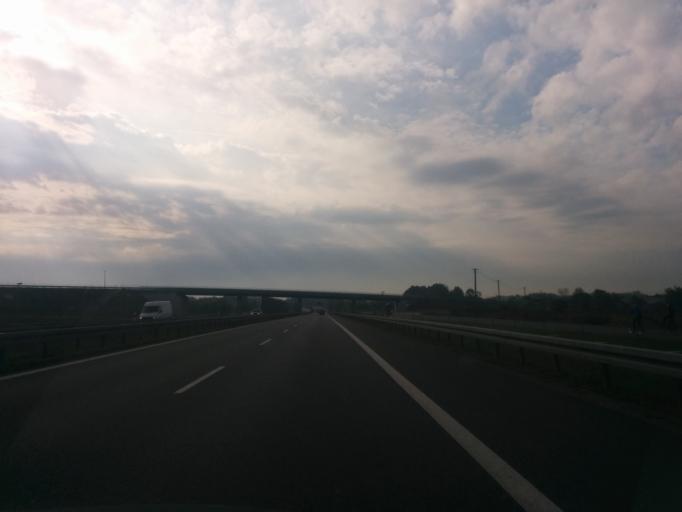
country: PL
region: Masovian Voivodeship
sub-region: Powiat bialobrzeski
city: Stara Blotnica
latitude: 51.5861
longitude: 20.9983
